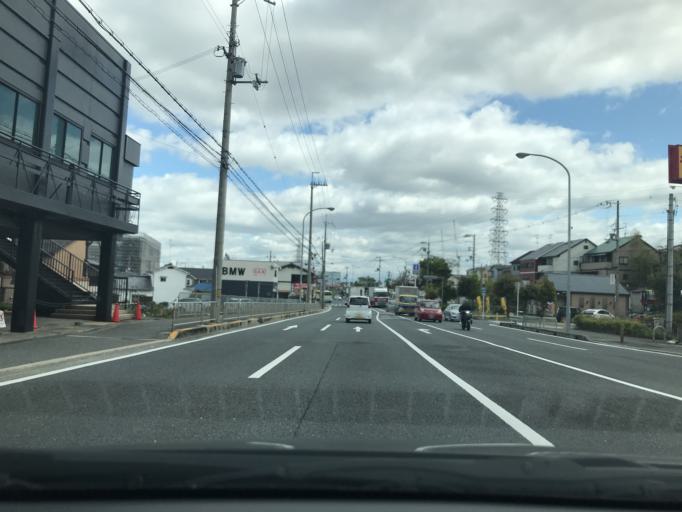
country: JP
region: Osaka
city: Ibaraki
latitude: 34.8365
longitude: 135.5477
